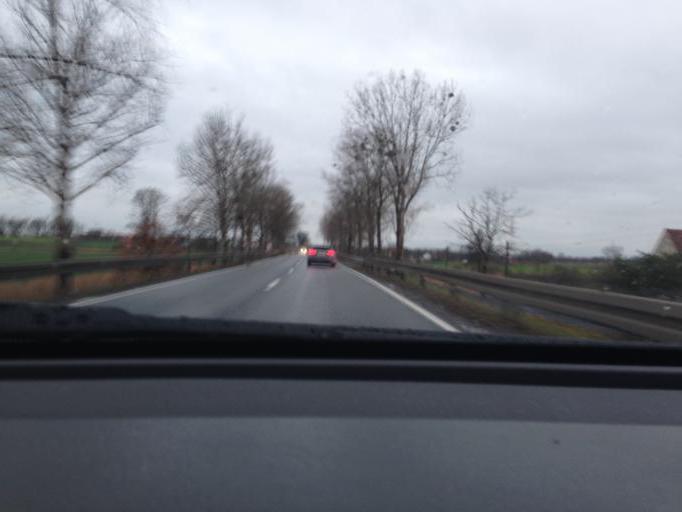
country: PL
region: Opole Voivodeship
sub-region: Powiat opolski
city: Opole
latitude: 50.7015
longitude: 17.9681
